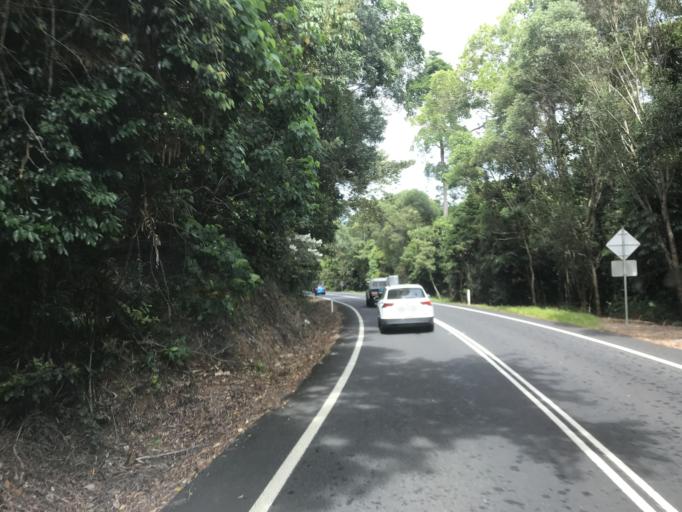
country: AU
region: Queensland
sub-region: Cassowary Coast
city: Innisfail
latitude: -17.8671
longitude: 146.0741
